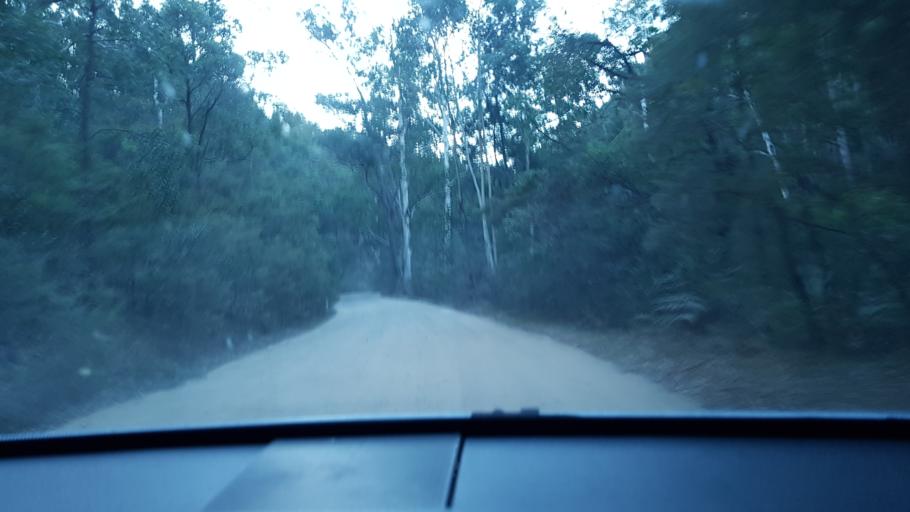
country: AU
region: New South Wales
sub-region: Lithgow
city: Lithgow
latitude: -33.1900
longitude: 150.2451
